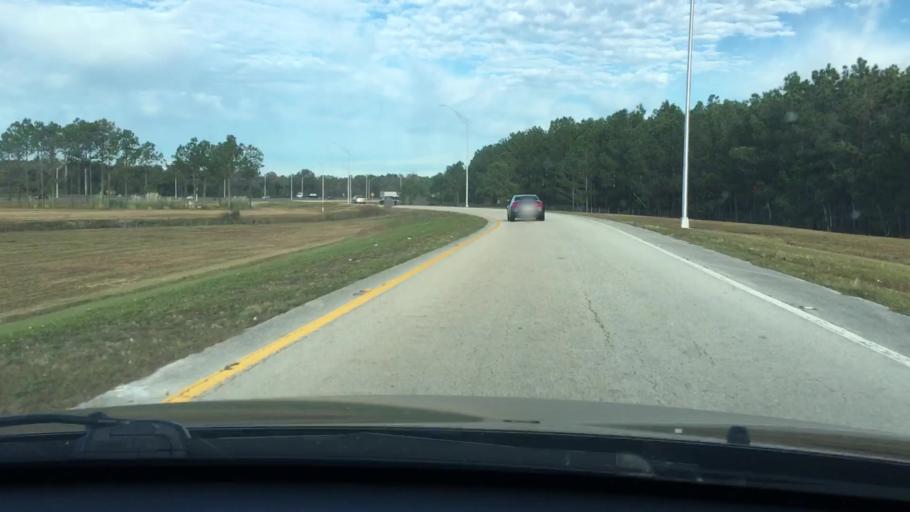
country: US
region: Florida
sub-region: Volusia County
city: Holly Hill
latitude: 29.2219
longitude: -81.1010
